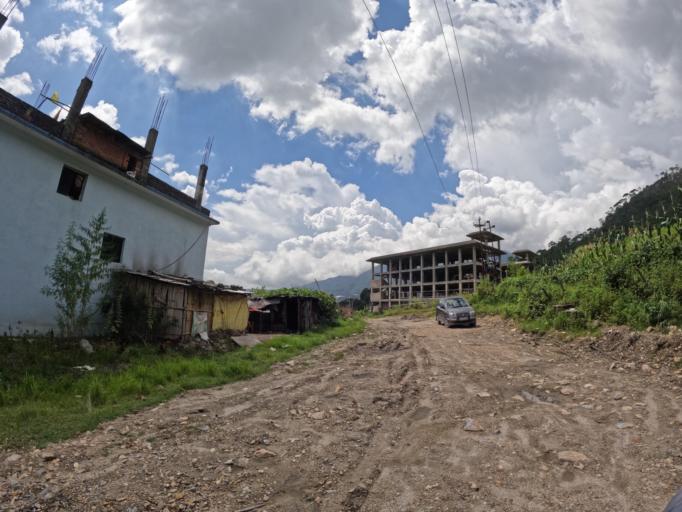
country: NP
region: Central Region
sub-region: Bagmati Zone
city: Kathmandu
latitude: 27.7785
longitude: 85.3355
